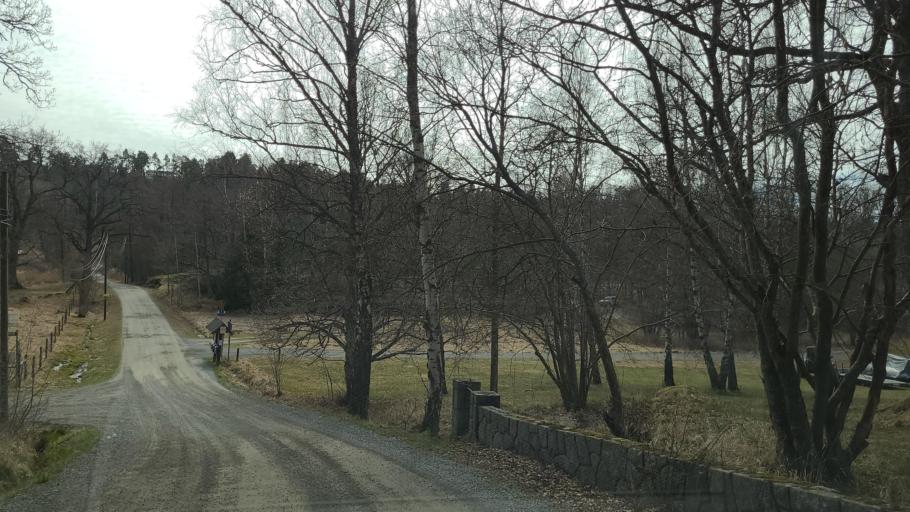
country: SE
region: Stockholm
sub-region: Varmdo Kommun
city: Hemmesta
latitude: 59.2822
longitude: 18.5480
